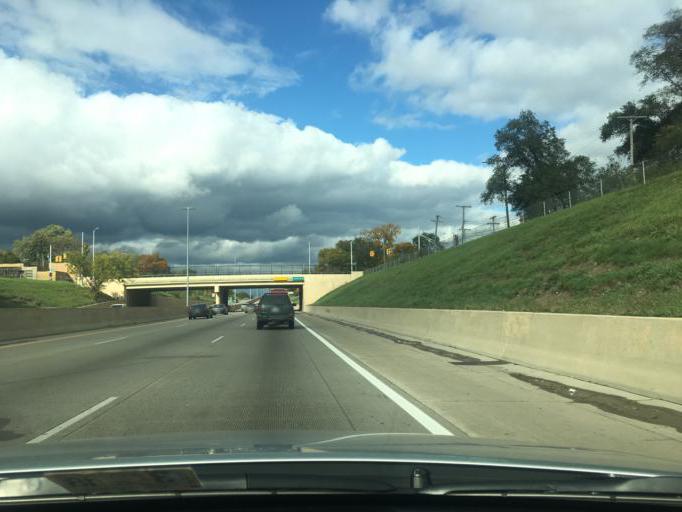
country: US
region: Michigan
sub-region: Oakland County
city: Southfield
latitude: 42.4215
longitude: -83.2189
